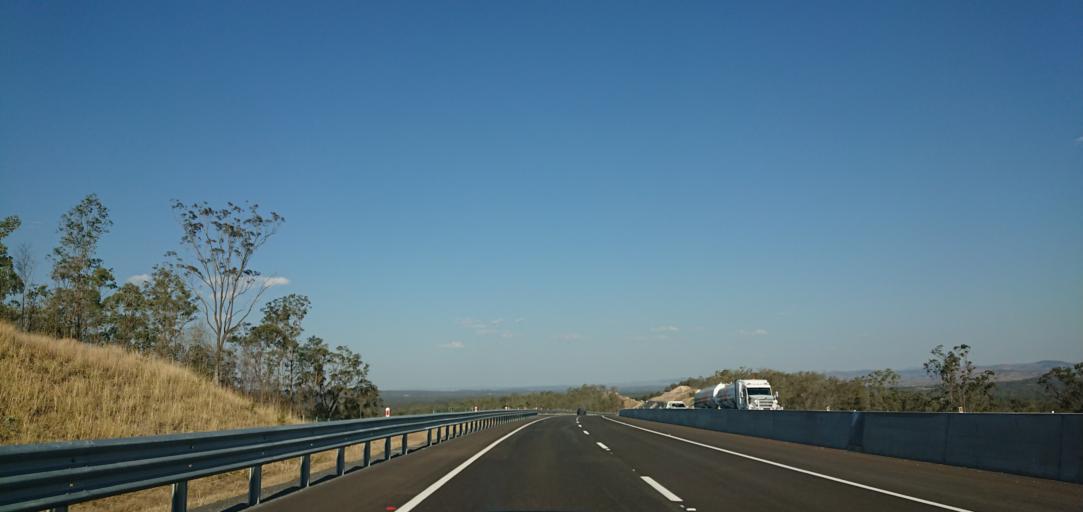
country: AU
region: Queensland
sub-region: Toowoomba
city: East Toowoomba
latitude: -27.5156
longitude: 152.0464
